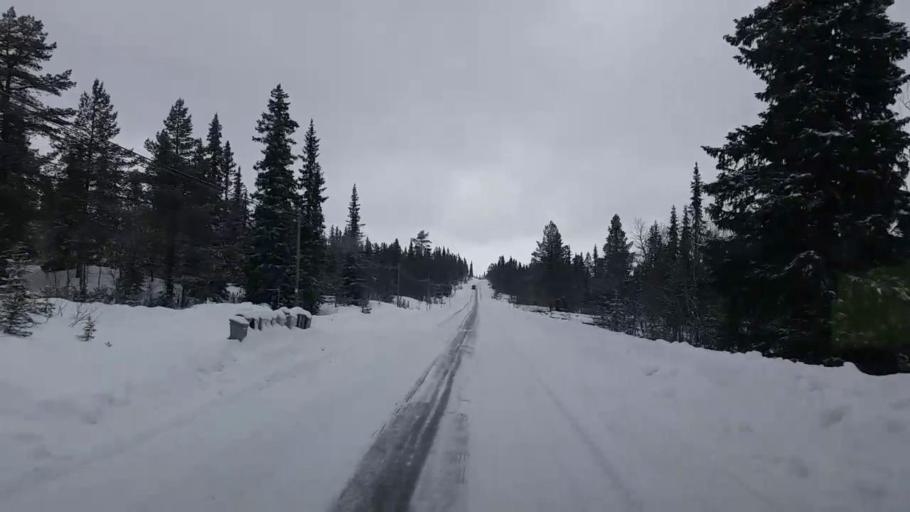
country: SE
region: Jaemtland
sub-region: Bergs Kommun
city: Hoverberg
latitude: 62.4854
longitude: 14.1204
